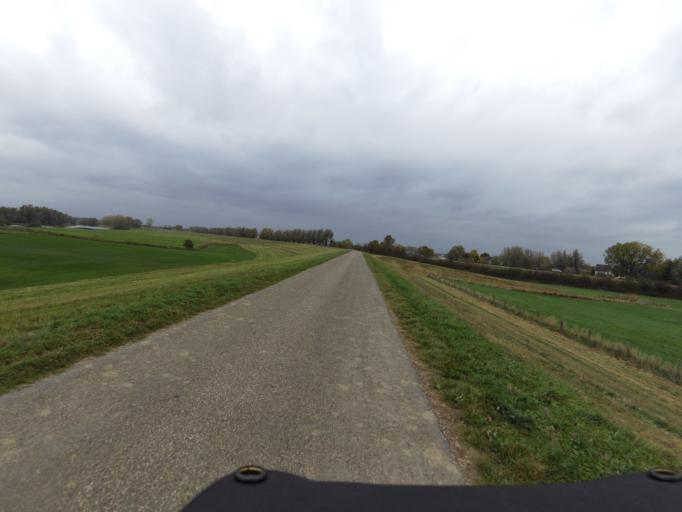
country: NL
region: Gelderland
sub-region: Gemeente Zevenaar
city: Zevenaar
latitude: 51.8725
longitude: 6.1017
